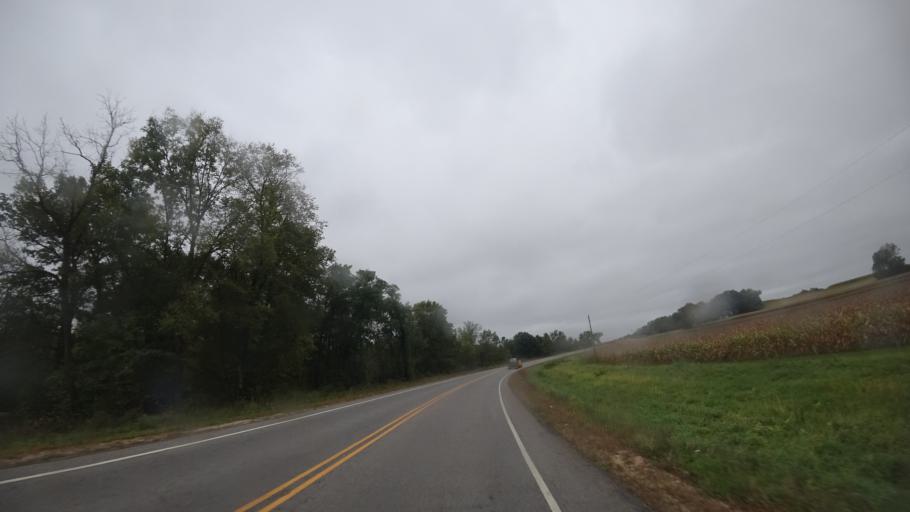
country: US
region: Wisconsin
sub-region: Crawford County
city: Prairie du Chien
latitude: 43.0342
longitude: -90.9891
